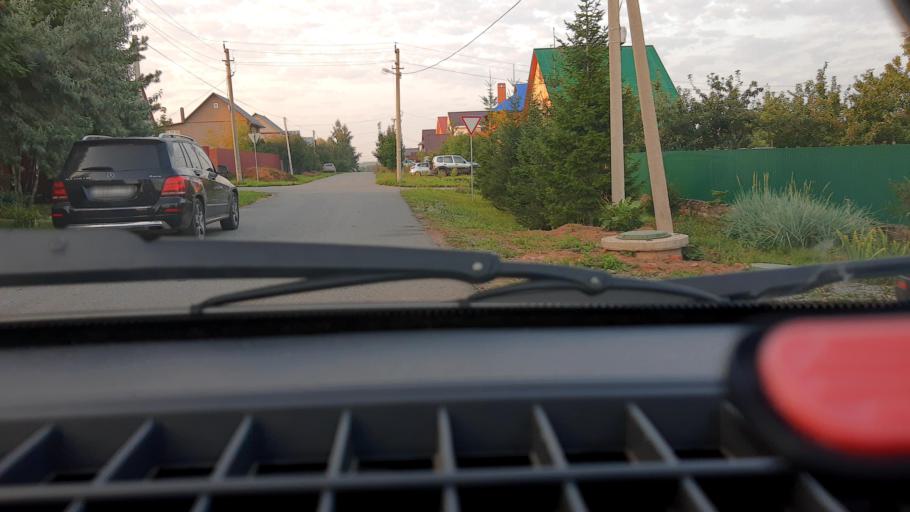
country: RU
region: Bashkortostan
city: Ufa
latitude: 54.5976
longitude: 55.9325
